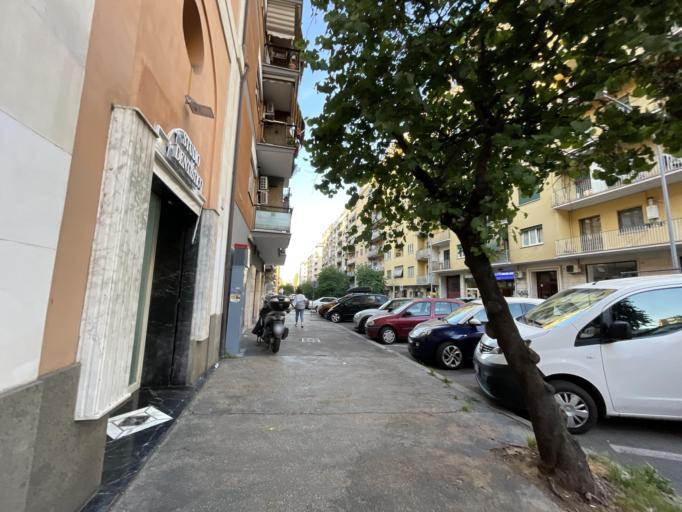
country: IT
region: Latium
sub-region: Citta metropolitana di Roma Capitale
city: Rome
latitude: 41.8768
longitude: 12.5223
